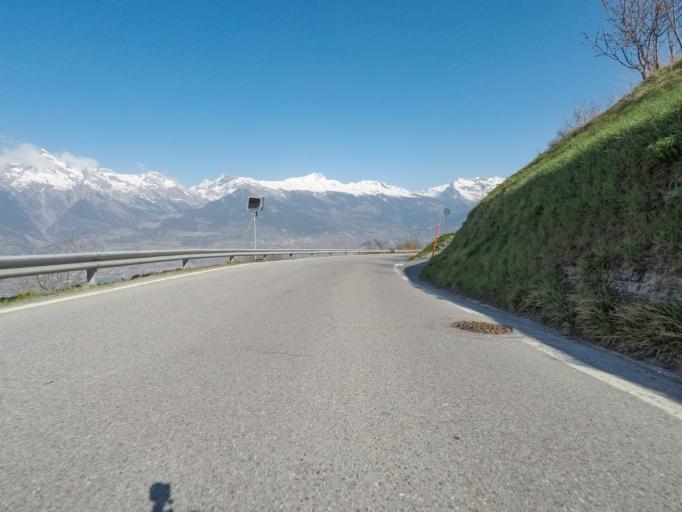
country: CH
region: Valais
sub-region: Conthey District
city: Basse-Nendaz
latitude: 46.1939
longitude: 7.3334
